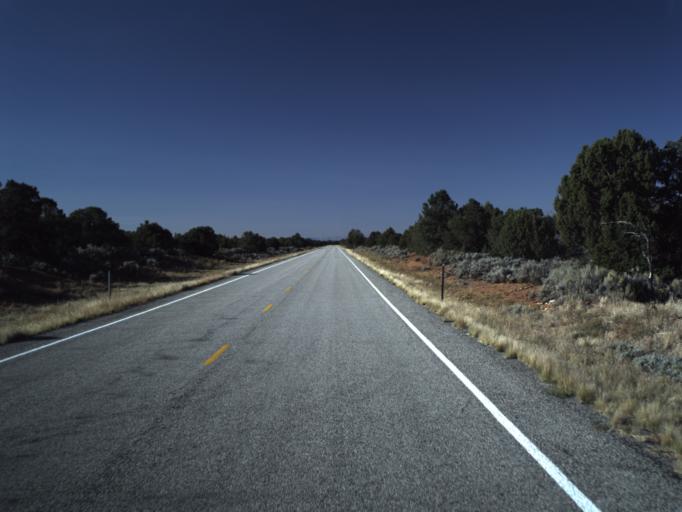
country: US
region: Utah
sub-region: San Juan County
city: Blanding
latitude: 37.5670
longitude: -109.9266
